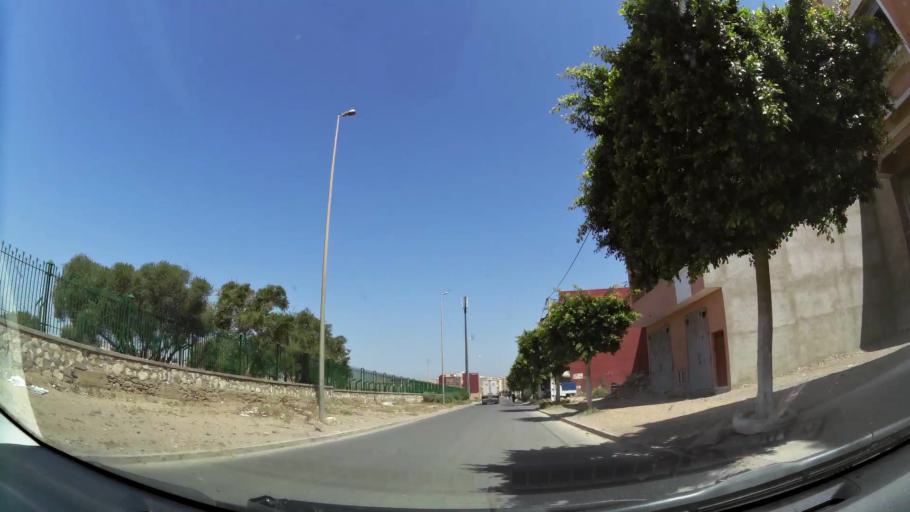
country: MA
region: Souss-Massa-Draa
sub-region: Inezgane-Ait Mellou
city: Inezgane
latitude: 30.3304
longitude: -9.5004
